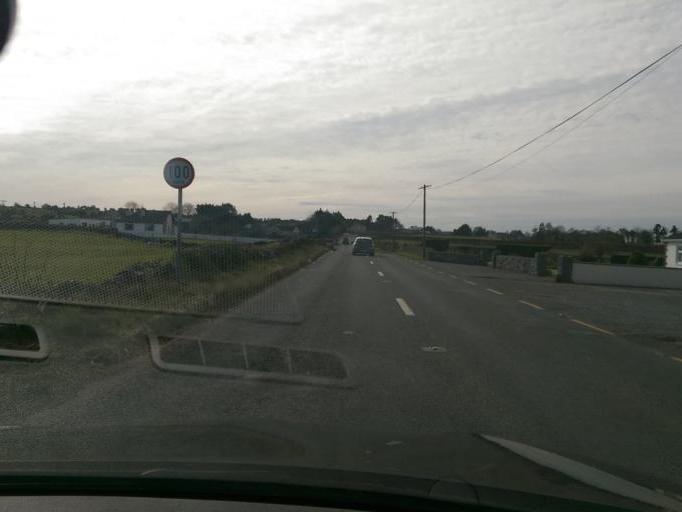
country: IE
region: Connaught
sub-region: County Galway
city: Tuam
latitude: 53.4146
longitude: -8.8008
